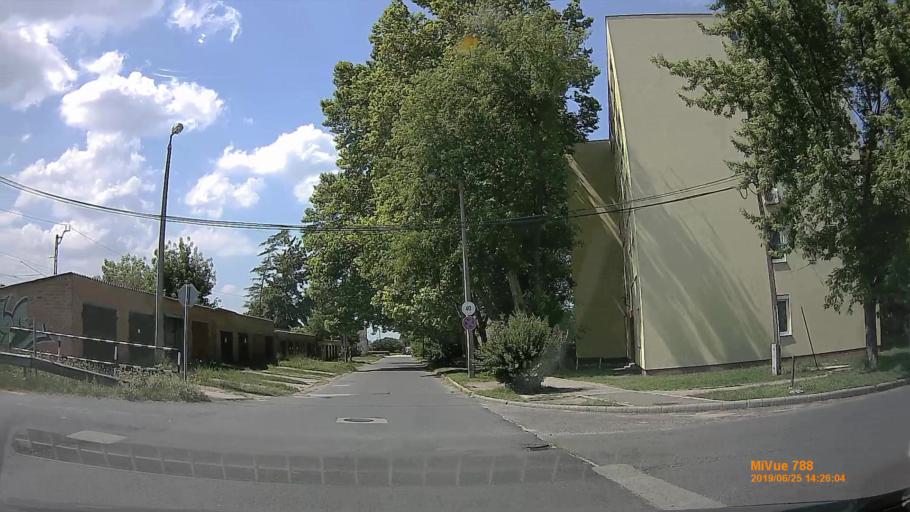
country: HU
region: Komarom-Esztergom
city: Dorog
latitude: 47.7177
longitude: 18.7420
